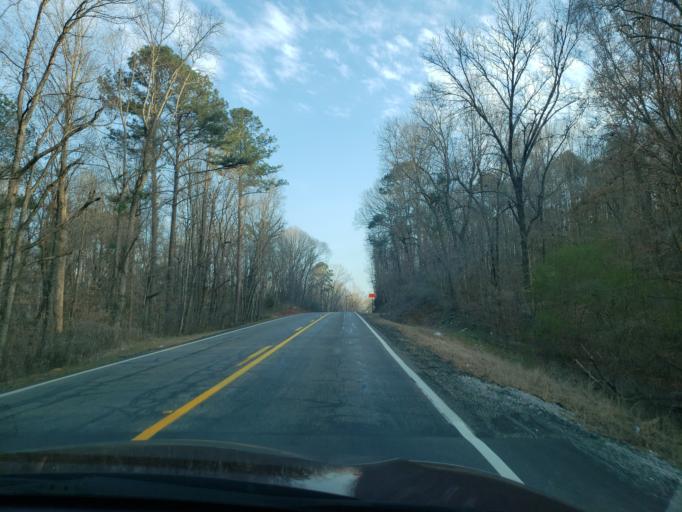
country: US
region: Alabama
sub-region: Hale County
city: Greensboro
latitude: 32.8121
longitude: -87.5958
